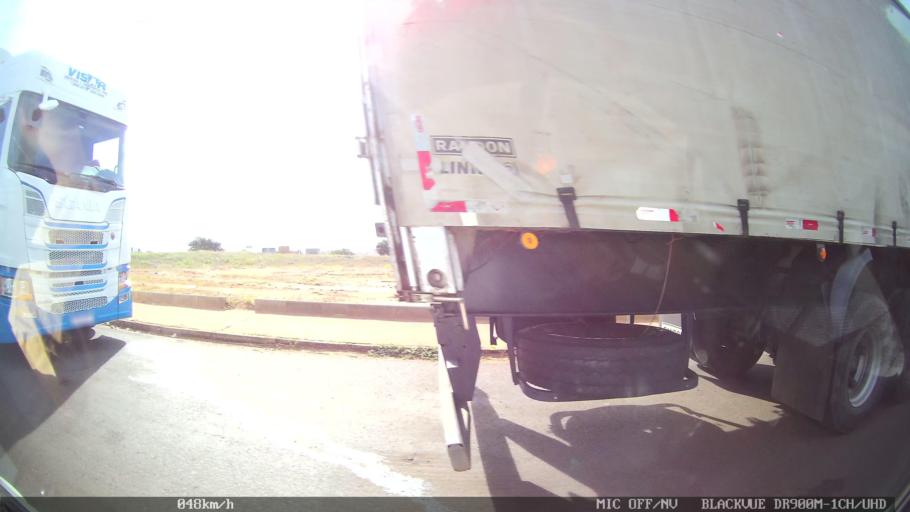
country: BR
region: Sao Paulo
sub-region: Sao Jose Do Rio Preto
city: Sao Jose do Rio Preto
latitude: -20.7983
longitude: -49.3299
